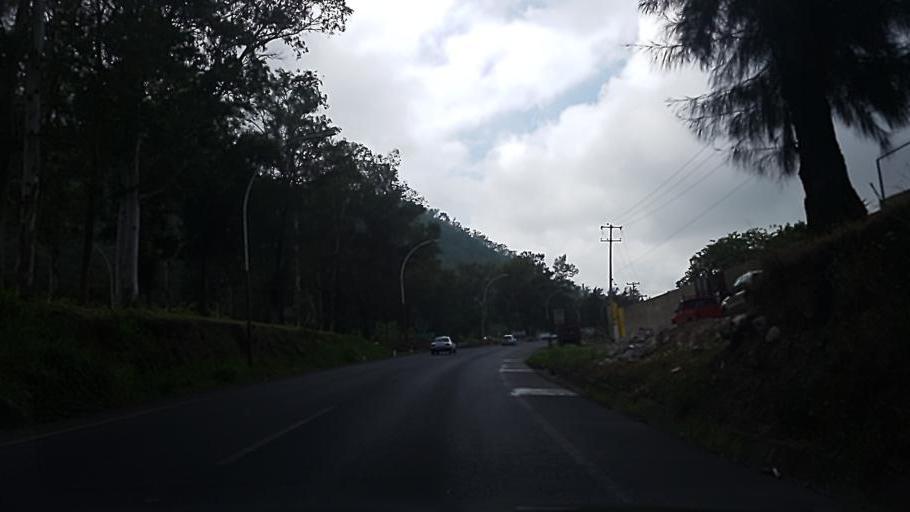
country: MX
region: Nayarit
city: Tepic
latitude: 21.5025
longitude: -104.9191
